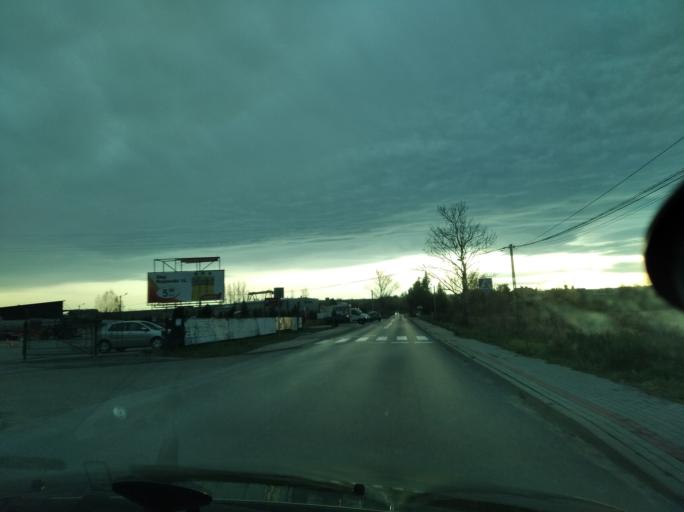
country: PL
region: Subcarpathian Voivodeship
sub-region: Powiat rzeszowski
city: Niechobrz
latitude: 50.0213
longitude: 21.8822
